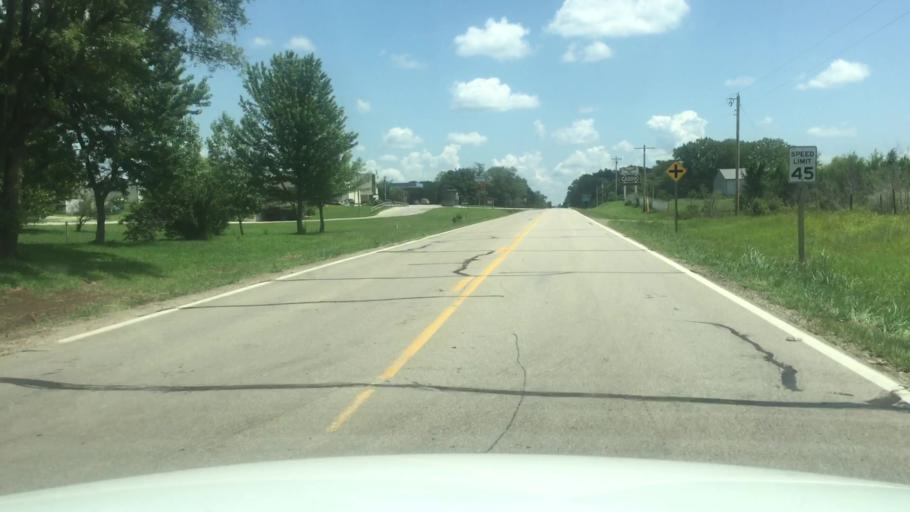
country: US
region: Kansas
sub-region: Brown County
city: Horton
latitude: 39.6674
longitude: -95.6424
